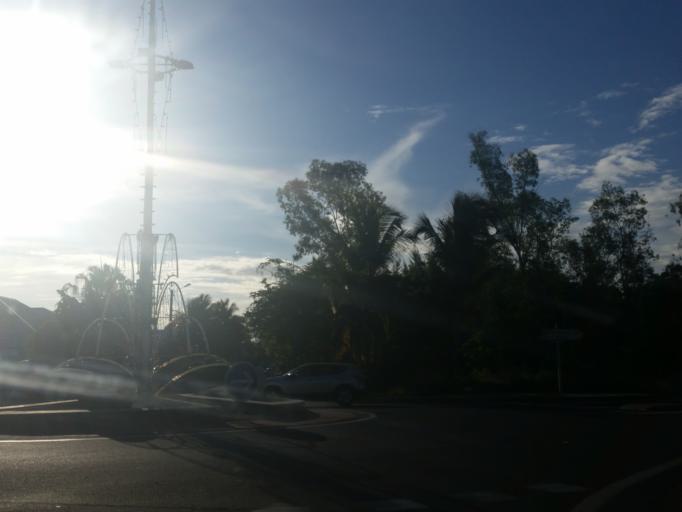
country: RE
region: Reunion
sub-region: Reunion
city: Les Avirons
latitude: -21.2652
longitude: 55.3368
